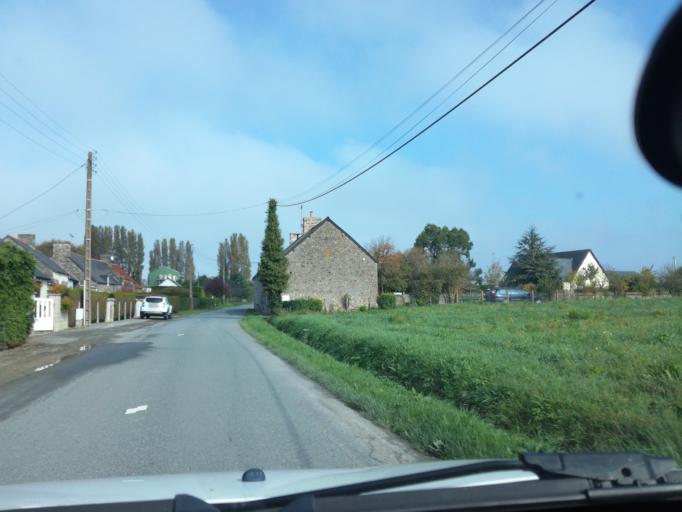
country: FR
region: Brittany
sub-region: Departement d'Ille-et-Vilaine
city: Cherrueix
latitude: 48.5962
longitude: -1.7167
